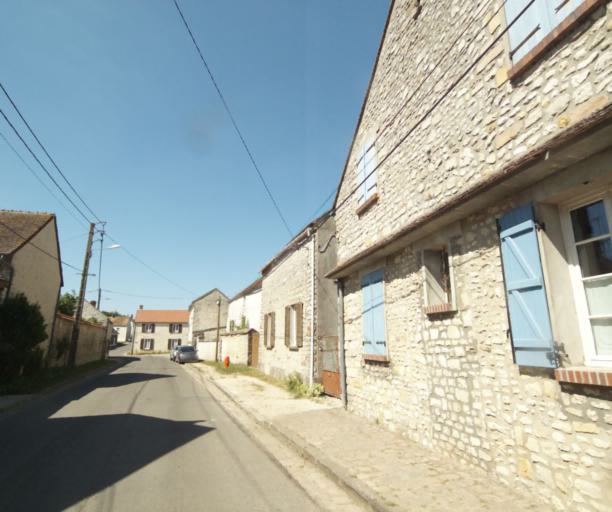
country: FR
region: Ile-de-France
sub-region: Departement de Seine-et-Marne
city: Acheres-la-Foret
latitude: 48.3445
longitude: 2.5649
